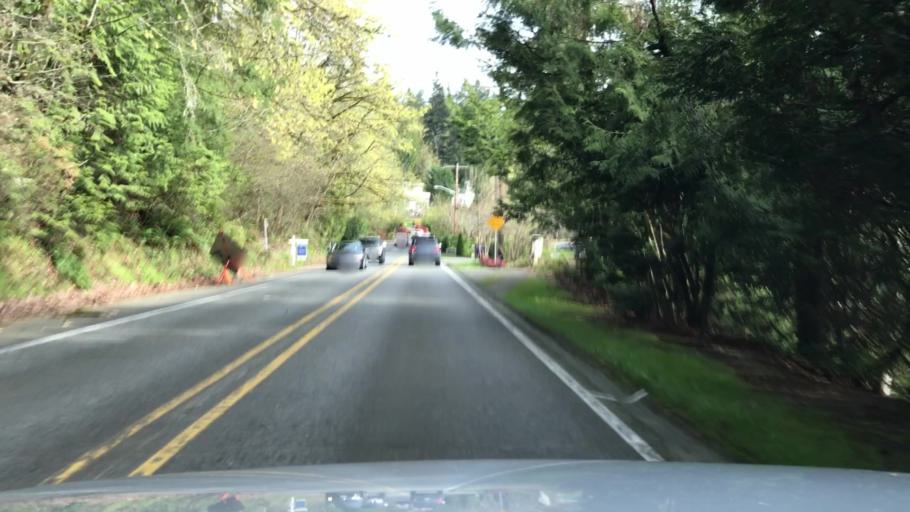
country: US
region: Washington
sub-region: King County
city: West Lake Sammamish
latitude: 47.6048
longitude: -122.1126
